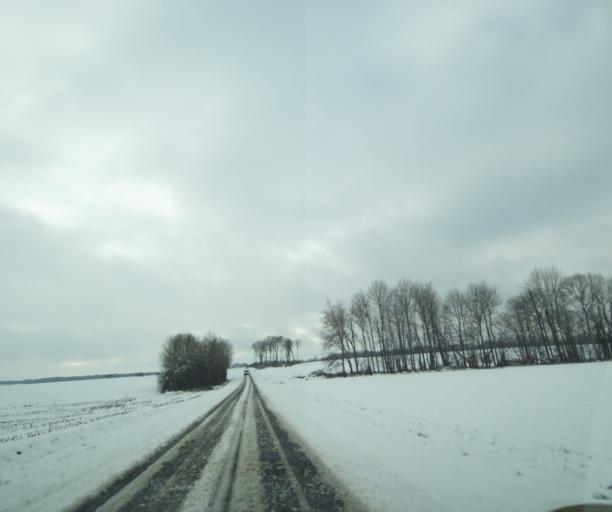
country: FR
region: Champagne-Ardenne
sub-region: Departement de la Haute-Marne
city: Montier-en-Der
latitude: 48.5044
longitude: 4.6867
